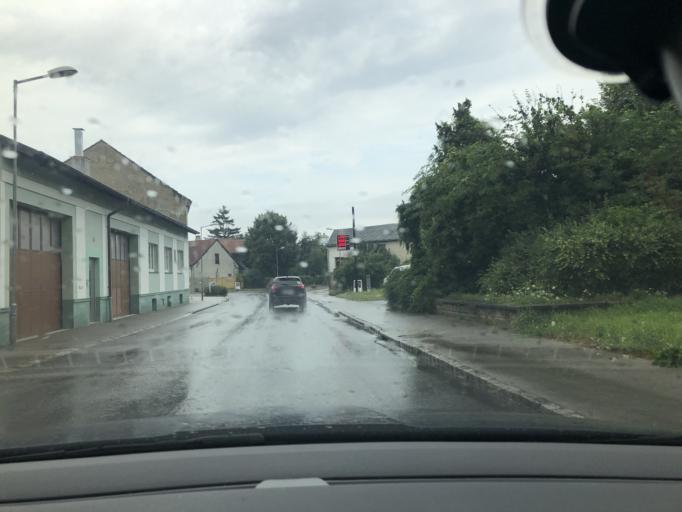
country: AT
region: Lower Austria
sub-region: Politischer Bezirk Ganserndorf
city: Auersthal
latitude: 48.3708
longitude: 16.6423
